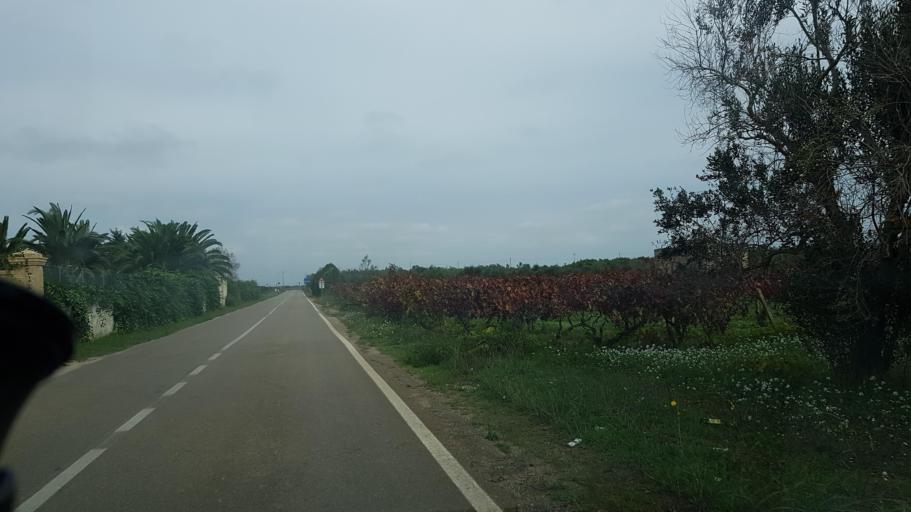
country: IT
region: Apulia
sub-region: Provincia di Lecce
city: Guagnano
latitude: 40.4178
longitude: 17.9497
